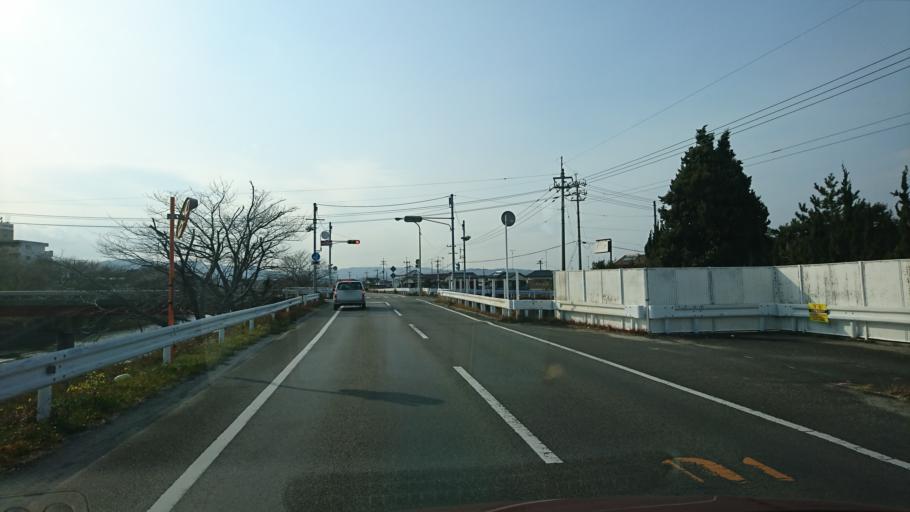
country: JP
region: Ehime
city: Saijo
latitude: 34.0379
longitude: 133.0286
